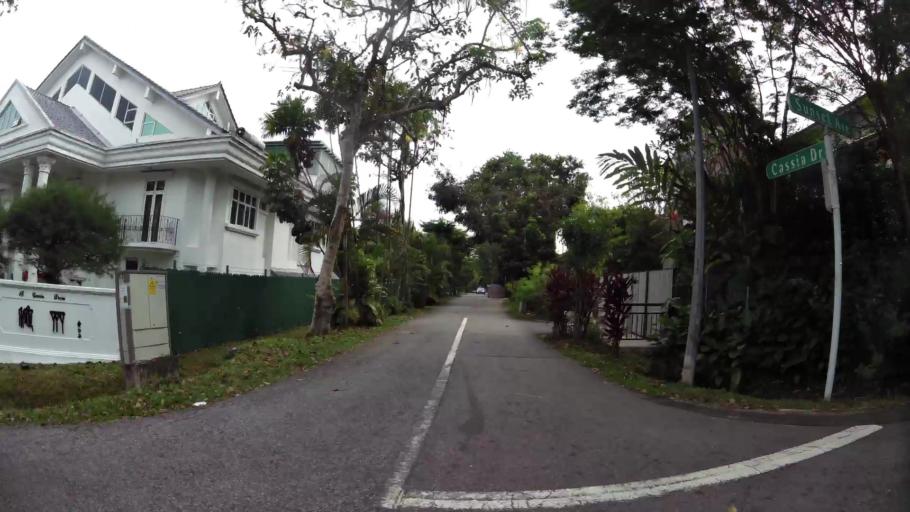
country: SG
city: Singapore
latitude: 1.3346
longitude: 103.8039
